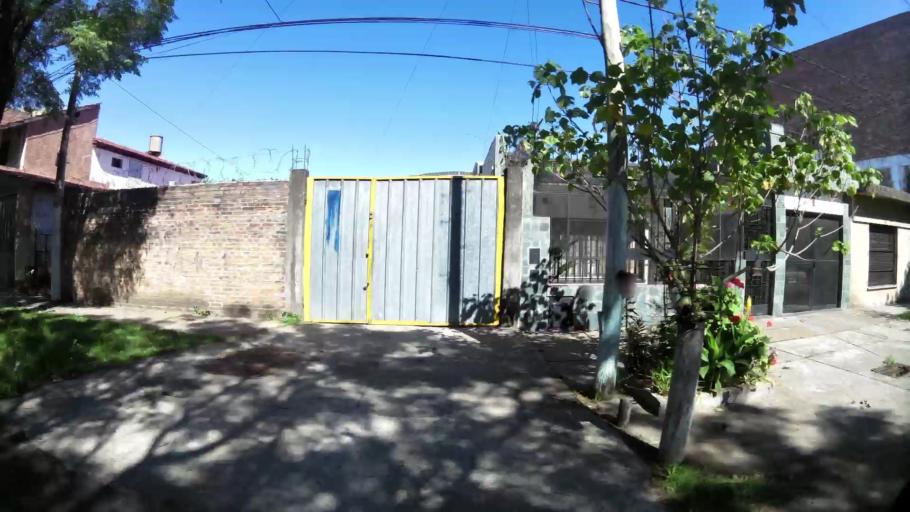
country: AR
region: Santa Fe
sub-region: Departamento de Rosario
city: Rosario
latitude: -32.9547
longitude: -60.6845
